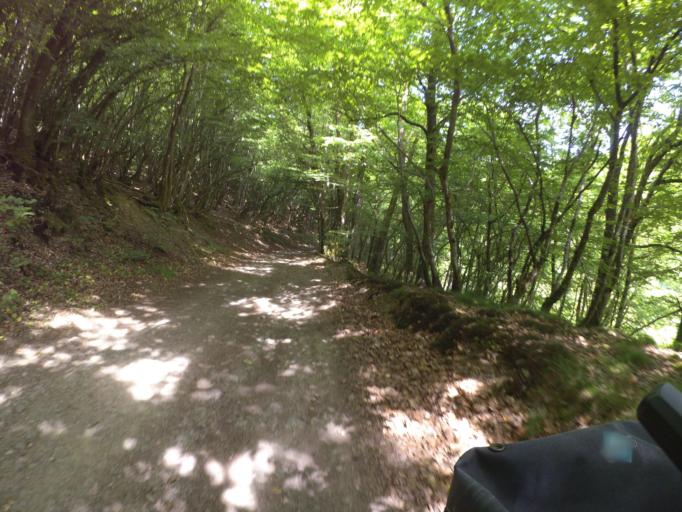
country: DE
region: Rheinland-Pfalz
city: Etgert
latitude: 49.7945
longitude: 7.0259
